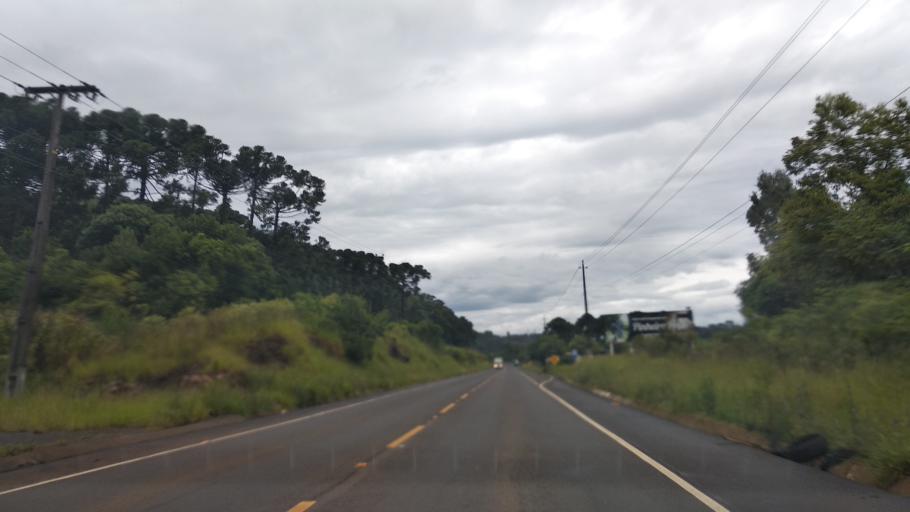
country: BR
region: Santa Catarina
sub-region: Videira
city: Videira
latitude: -27.0481
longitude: -51.1669
